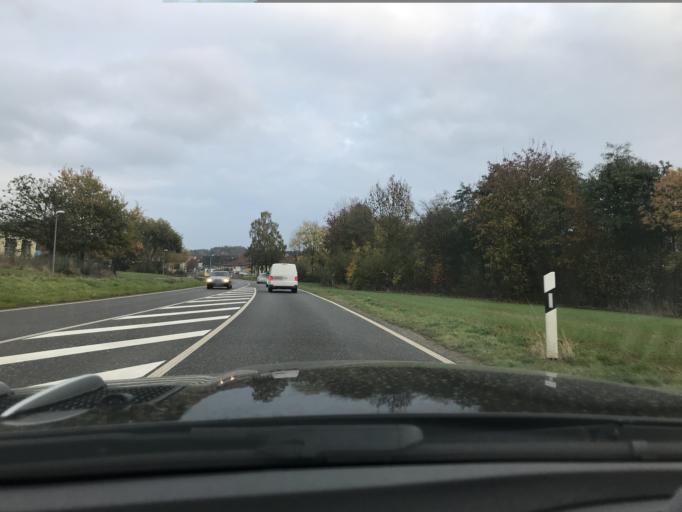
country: DE
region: Hesse
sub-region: Regierungsbezirk Kassel
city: Immenhausen
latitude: 51.4310
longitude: 9.4653
